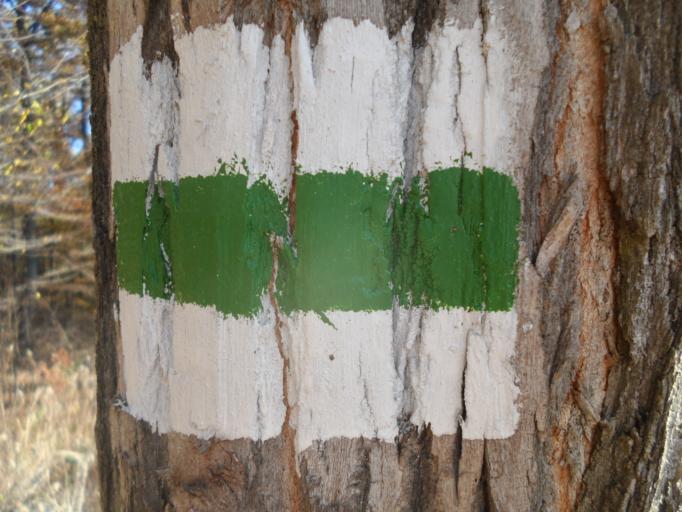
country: HU
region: Veszprem
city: Ajka
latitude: 47.2007
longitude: 17.5742
